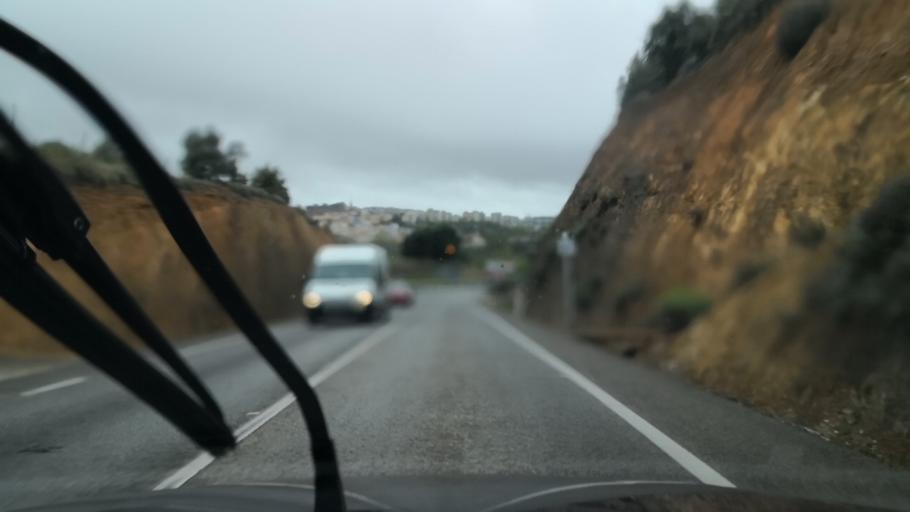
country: ES
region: Extremadura
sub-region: Provincia de Caceres
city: Caceres
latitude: 39.4874
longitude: -6.3830
